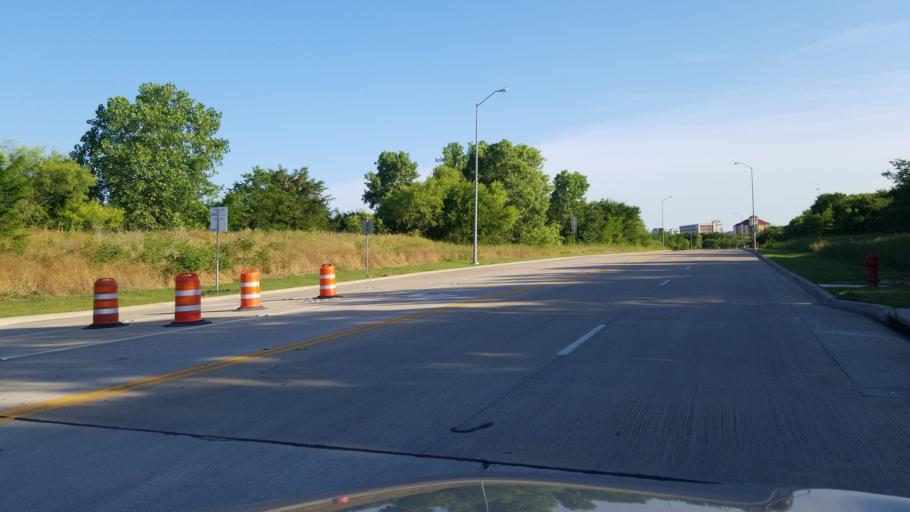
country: US
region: Texas
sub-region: Dallas County
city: Grand Prairie
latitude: 32.6817
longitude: -97.0289
